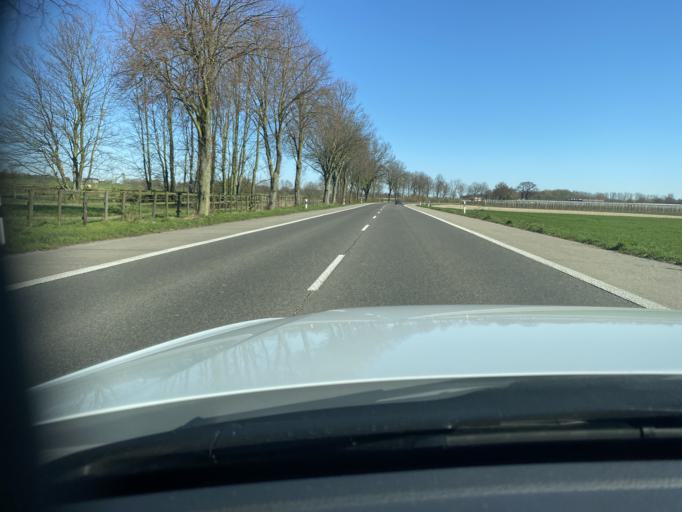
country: DE
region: North Rhine-Westphalia
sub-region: Regierungsbezirk Dusseldorf
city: Neubrueck
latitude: 51.1410
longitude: 6.6466
